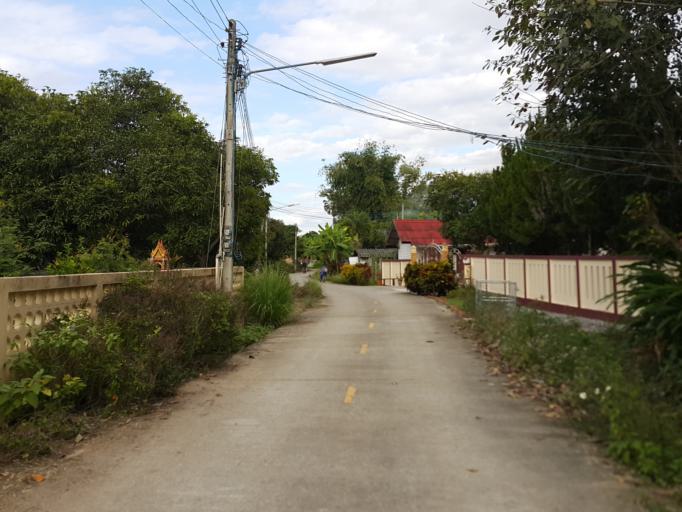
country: TH
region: Chiang Mai
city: San Sai
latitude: 18.8721
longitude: 99.0997
